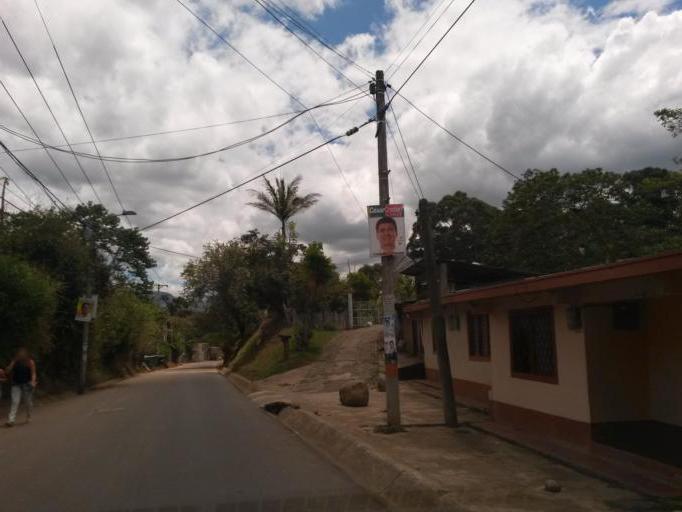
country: CO
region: Cauca
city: Popayan
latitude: 2.4794
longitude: -76.5675
